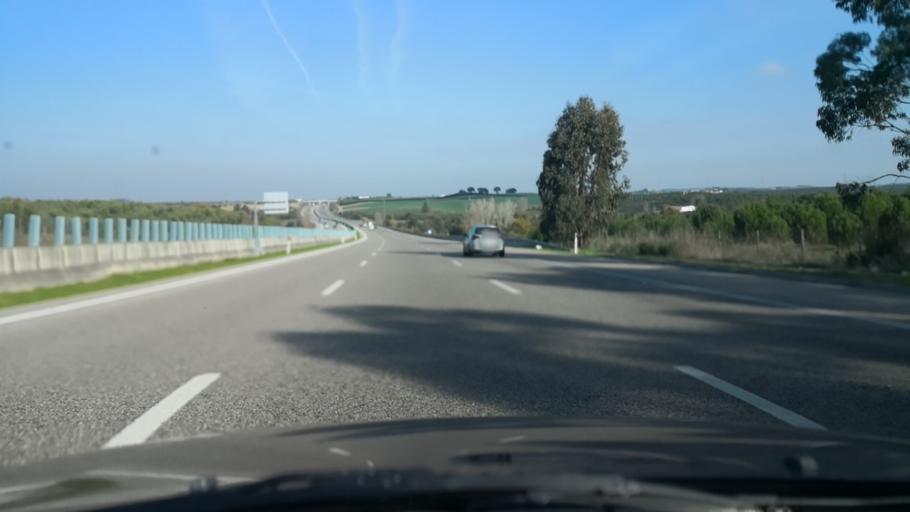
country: PT
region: Santarem
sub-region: Santarem
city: Santarem
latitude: 39.3157
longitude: -8.6680
